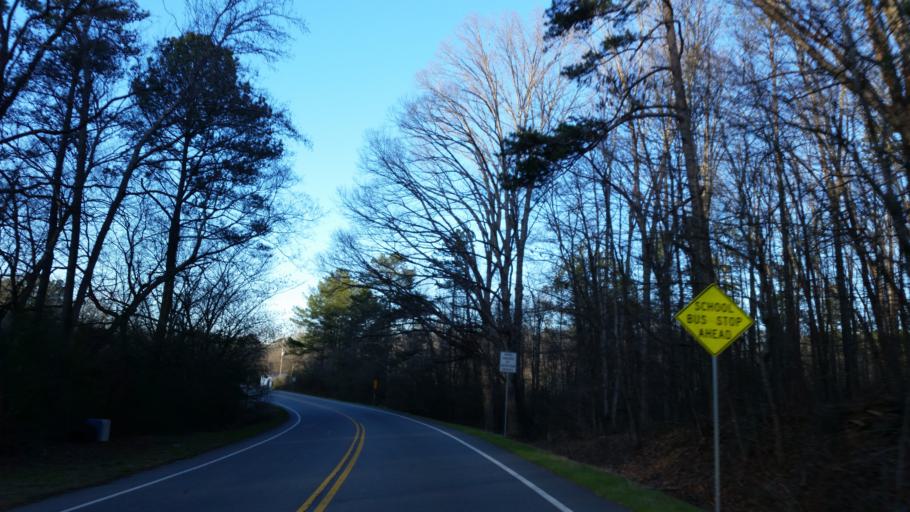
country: US
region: Georgia
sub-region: Gordon County
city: Calhoun
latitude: 34.6172
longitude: -84.9488
